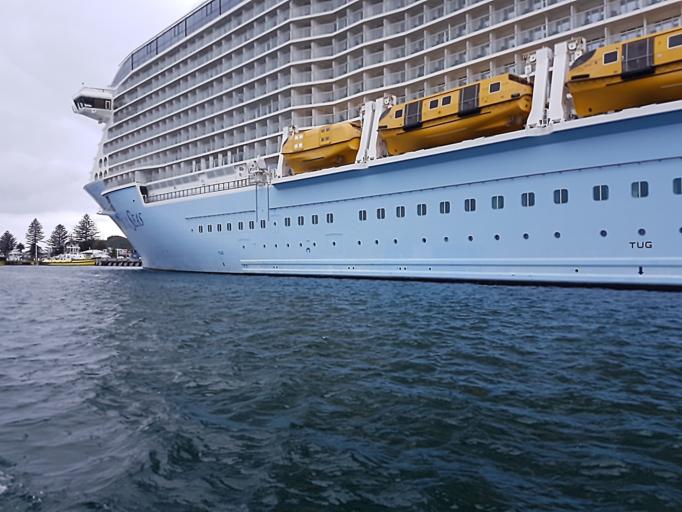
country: NZ
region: Bay of Plenty
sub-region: Tauranga City
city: Tauranga
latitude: -37.6439
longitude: 176.1811
